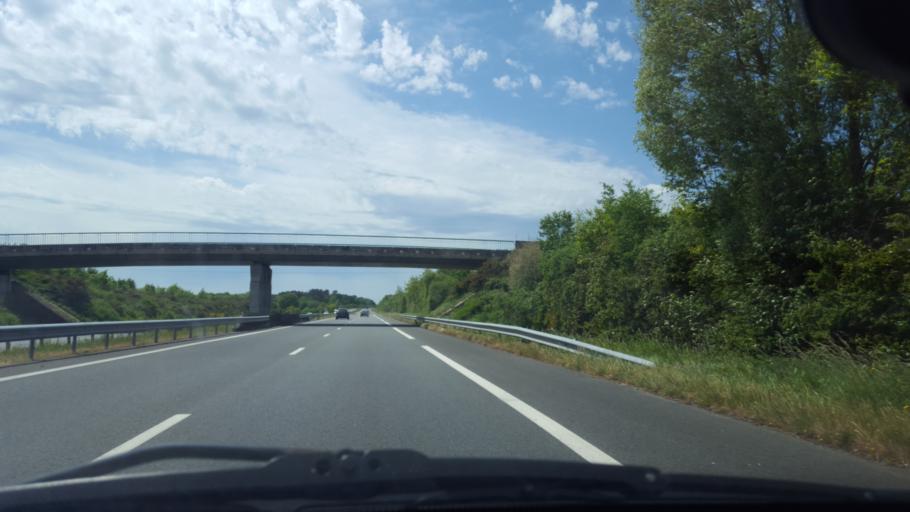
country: FR
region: Pays de la Loire
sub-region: Departement de la Loire-Atlantique
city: Saint-Lumine-de-Coutais
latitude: 47.0174
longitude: -1.6963
